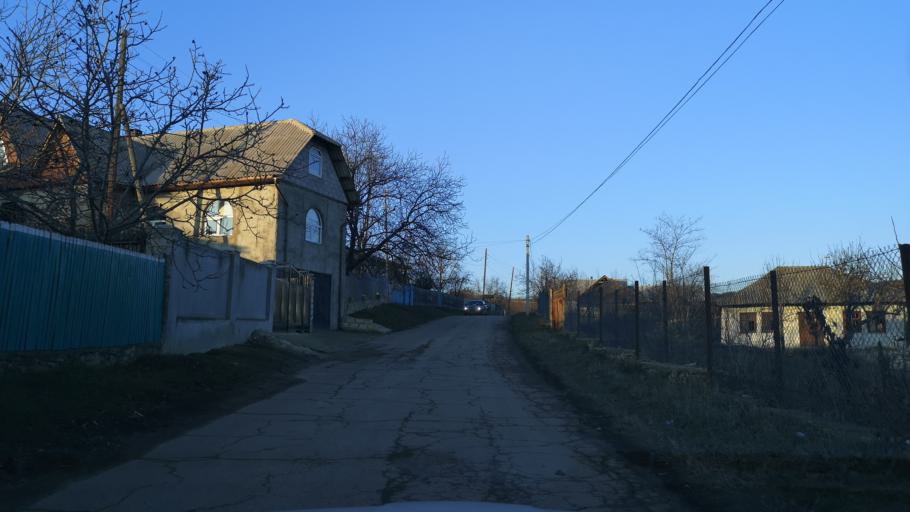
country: MD
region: Orhei
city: Orhei
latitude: 47.3644
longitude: 28.6901
